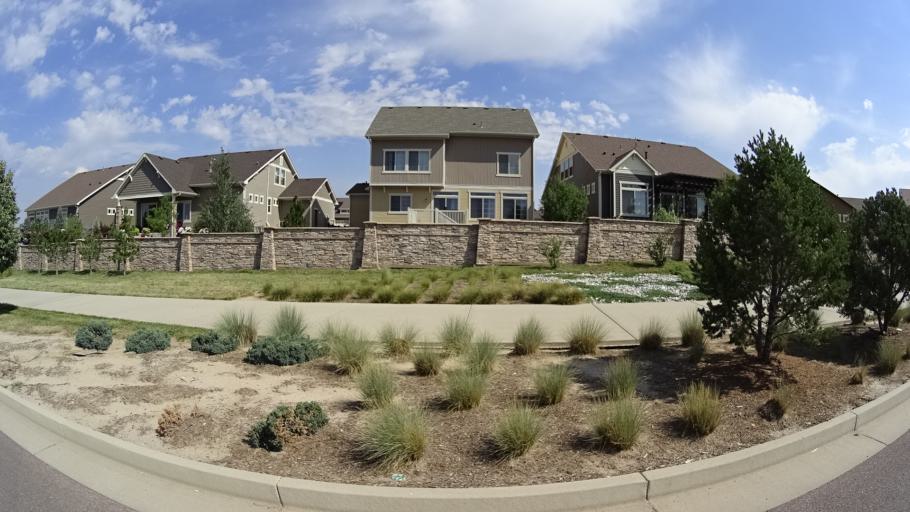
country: US
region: Colorado
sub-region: El Paso County
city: Cimarron Hills
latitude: 38.9268
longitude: -104.6797
